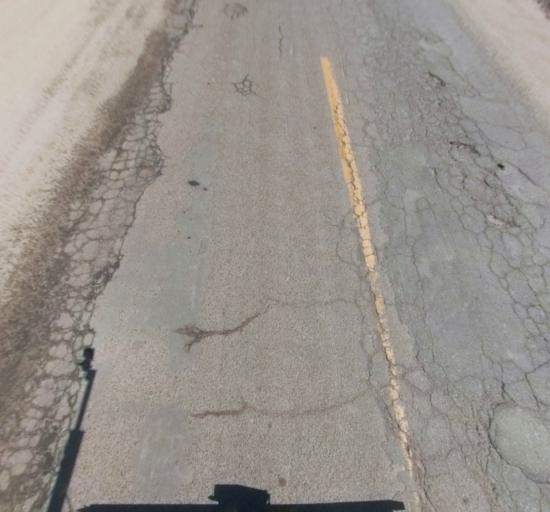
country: US
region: California
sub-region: Madera County
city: Chowchilla
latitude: 37.0696
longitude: -120.4010
